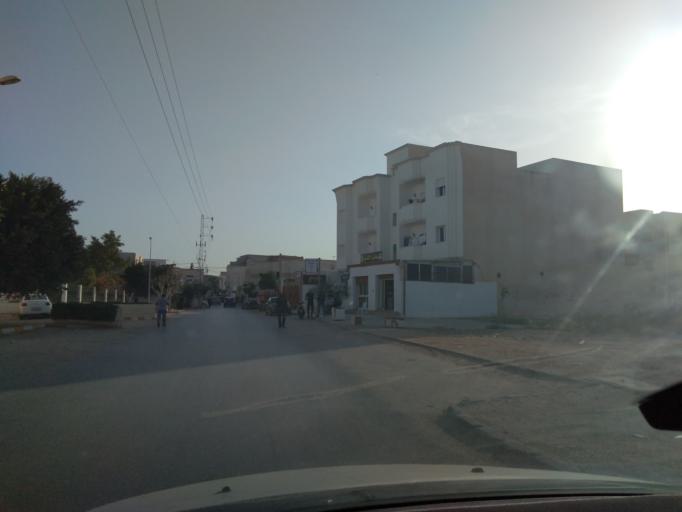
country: TN
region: Manouba
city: Manouba
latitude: 36.7948
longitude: 10.0892
